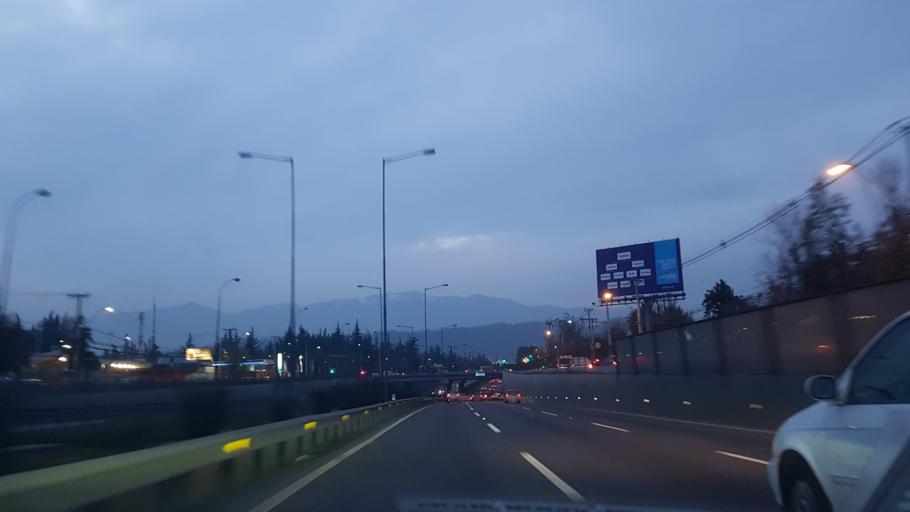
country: CL
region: Santiago Metropolitan
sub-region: Provincia de Santiago
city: Santiago
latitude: -33.3819
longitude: -70.6427
